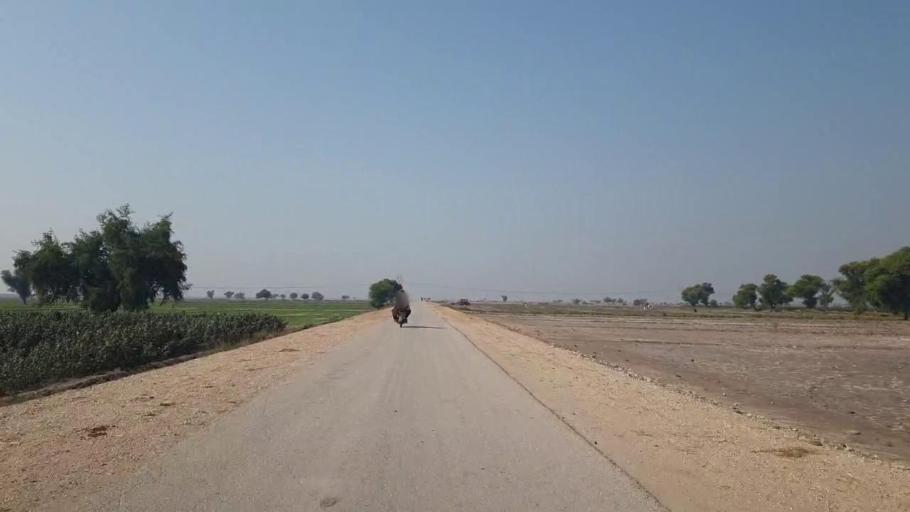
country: PK
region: Sindh
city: Sehwan
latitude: 26.4190
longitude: 67.8197
